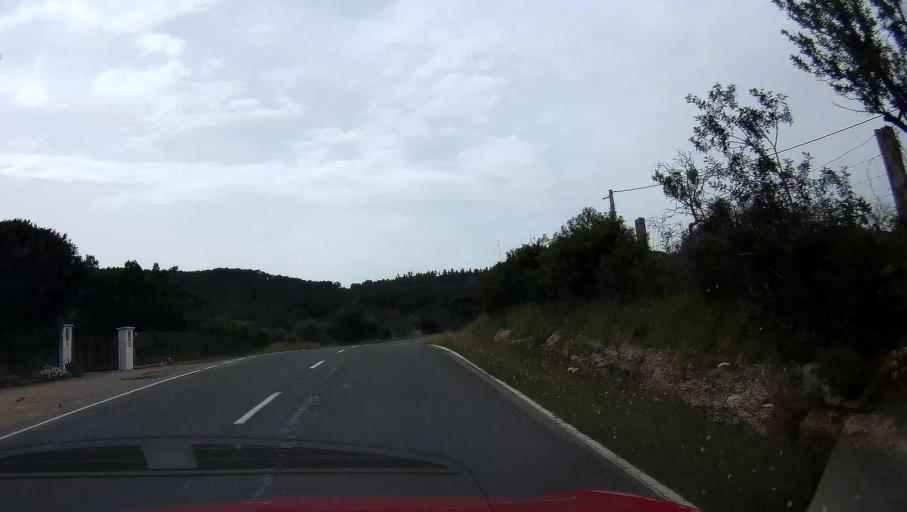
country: ES
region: Balearic Islands
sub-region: Illes Balears
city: Sant Joan de Labritja
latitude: 39.0872
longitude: 1.5016
